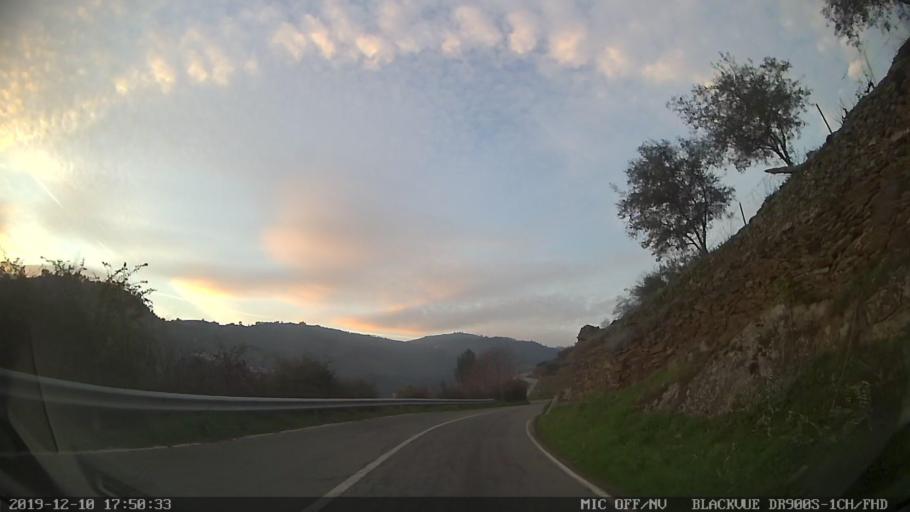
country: PT
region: Vila Real
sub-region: Sabrosa
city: Vilela
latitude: 41.2064
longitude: -7.5399
